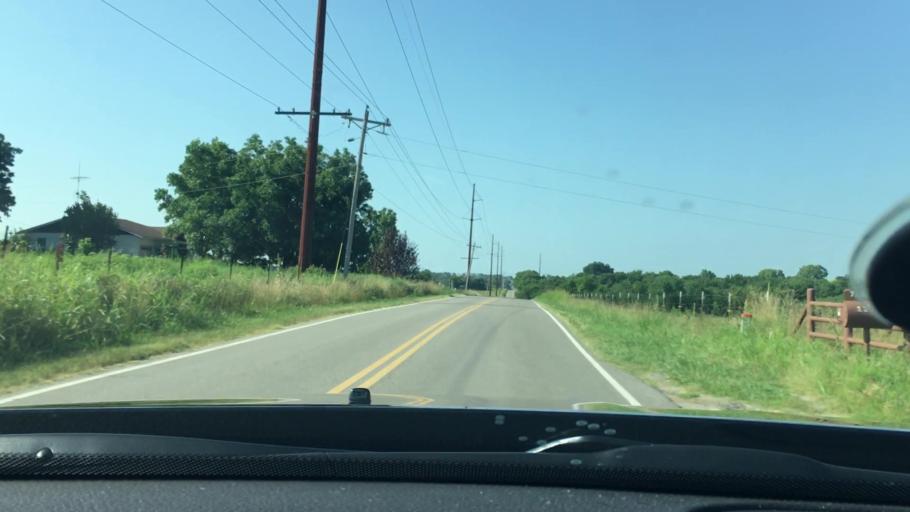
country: US
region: Oklahoma
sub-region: Pontotoc County
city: Ada
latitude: 34.8019
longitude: -96.6348
